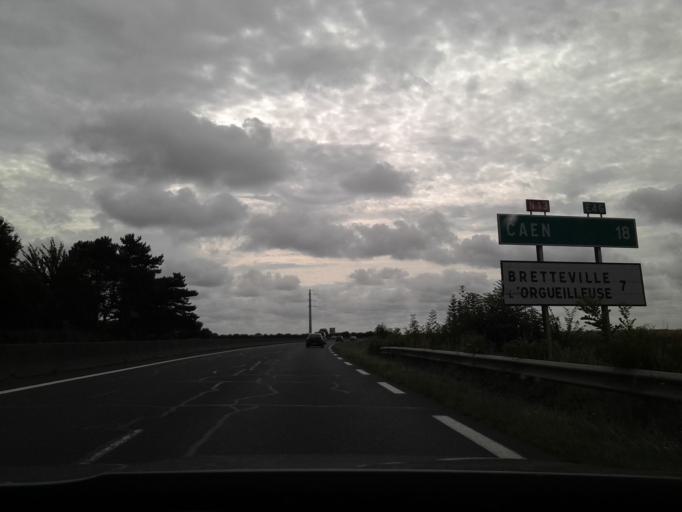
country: FR
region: Lower Normandy
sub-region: Departement du Calvados
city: Tilly-sur-Seulles
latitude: 49.2394
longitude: -0.5977
